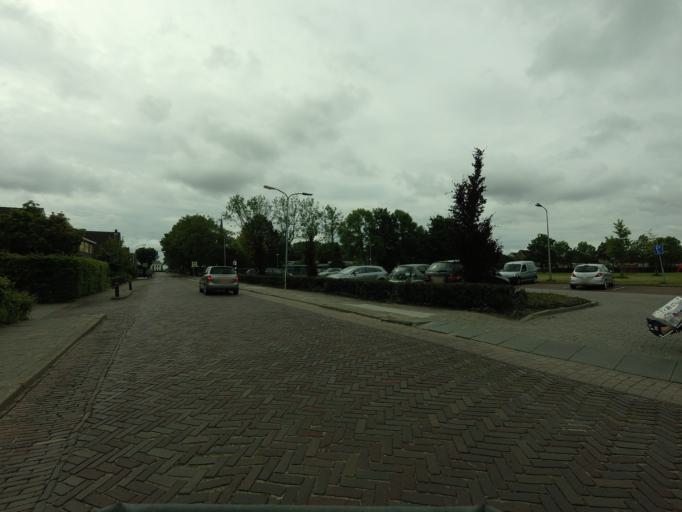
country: NL
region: North Holland
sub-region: Gemeente Hoorn
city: Hoorn
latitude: 52.6918
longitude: 5.0571
